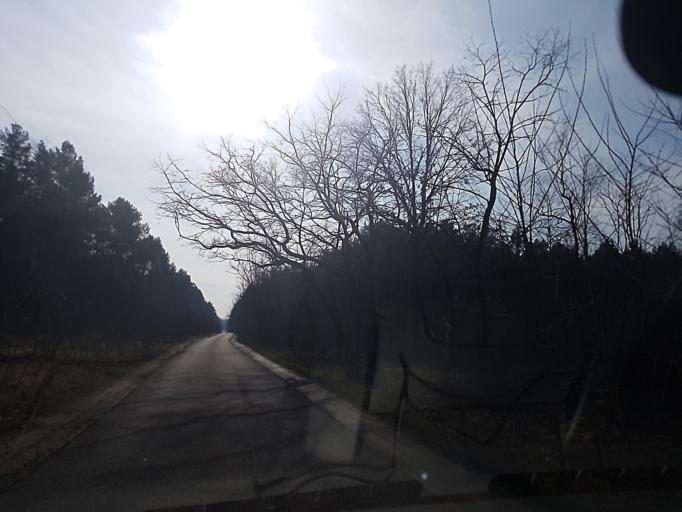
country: DE
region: Brandenburg
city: Wenzlow
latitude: 52.3343
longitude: 12.4392
